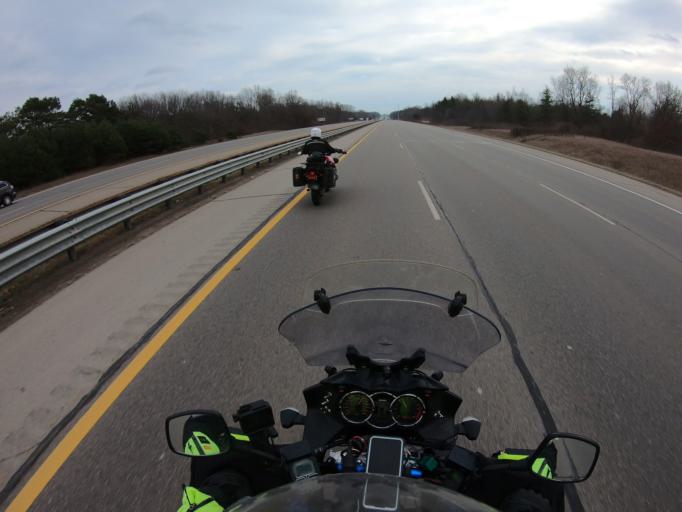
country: US
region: Michigan
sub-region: Oakland County
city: Holly
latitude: 42.8046
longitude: -83.5630
